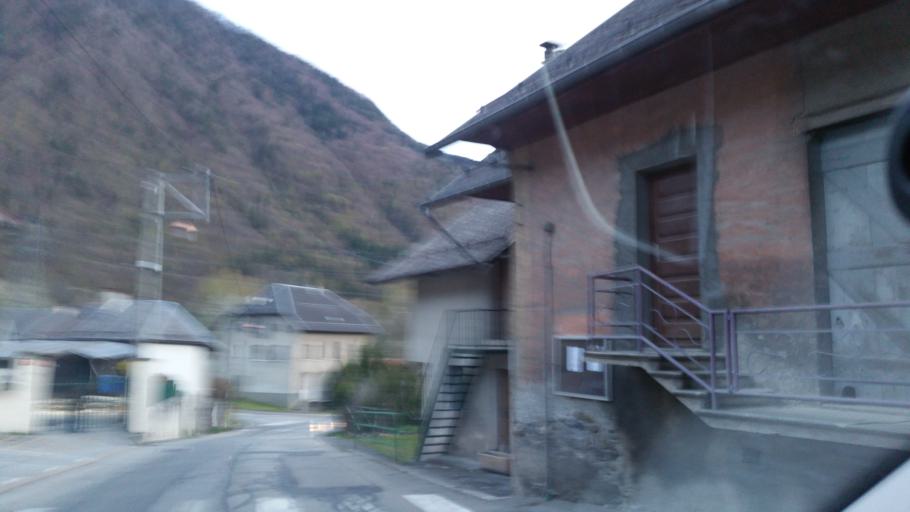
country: FR
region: Rhone-Alpes
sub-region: Departement de la Savoie
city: La Chambre
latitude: 45.3655
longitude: 6.3163
